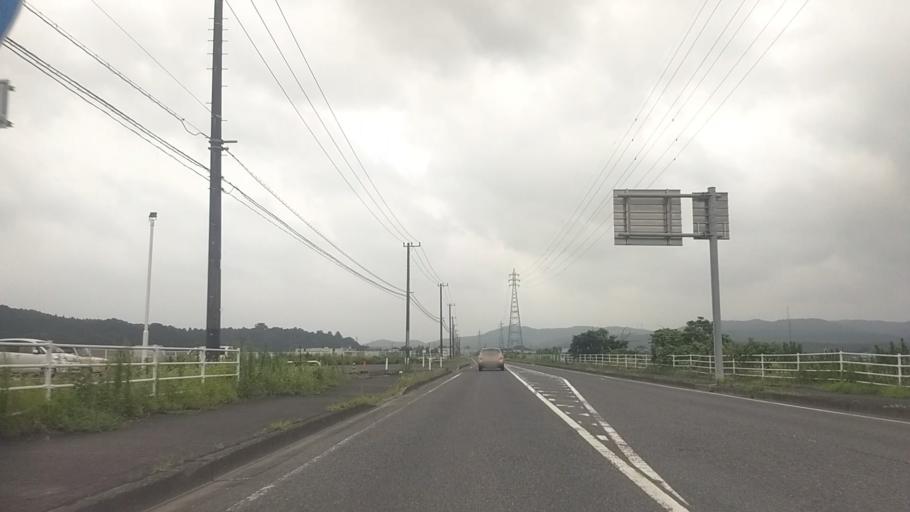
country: JP
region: Chiba
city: Kisarazu
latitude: 35.3301
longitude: 140.0550
